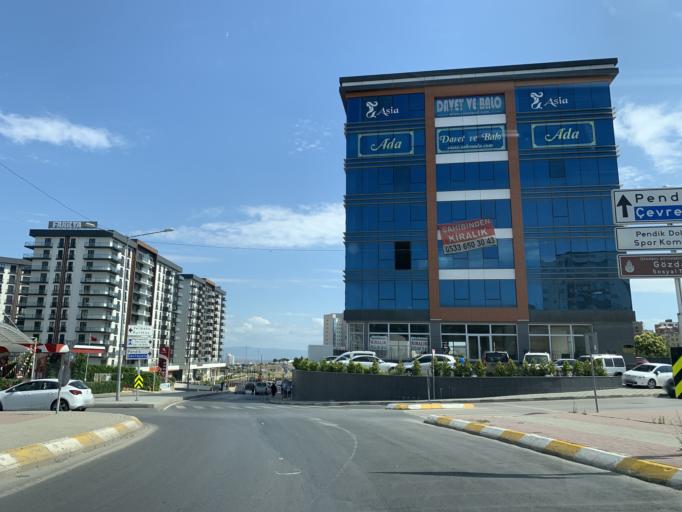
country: TR
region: Istanbul
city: Pendik
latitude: 40.8915
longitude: 29.2627
